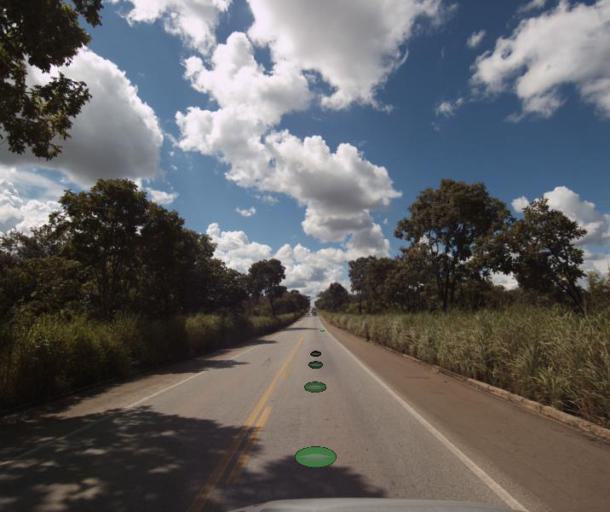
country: BR
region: Goias
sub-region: Porangatu
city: Porangatu
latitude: -13.6251
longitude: -49.0427
